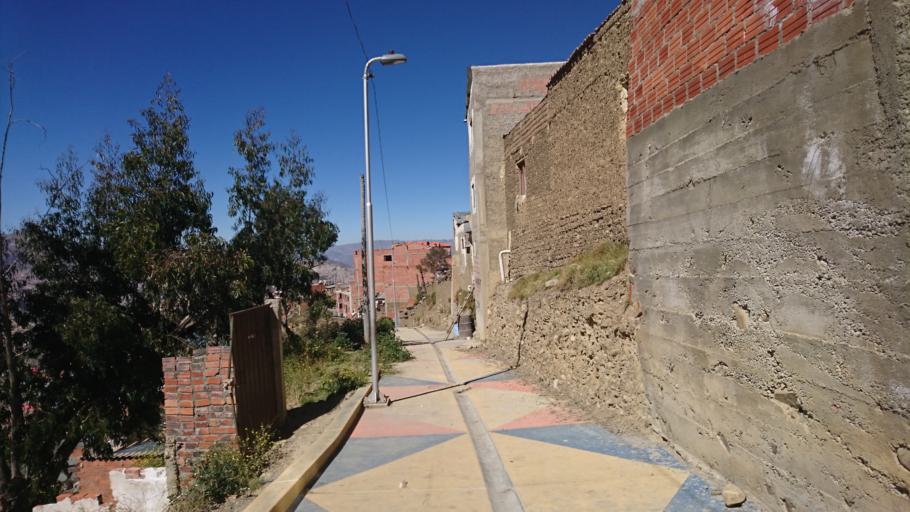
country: BO
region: La Paz
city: La Paz
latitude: -16.4909
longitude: -68.1031
